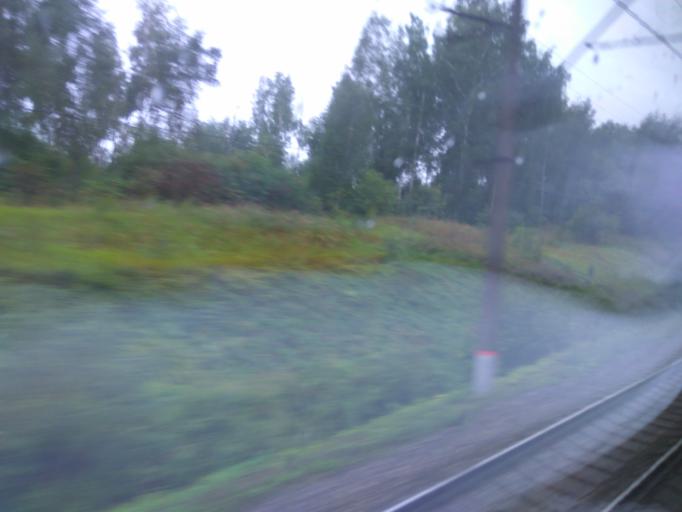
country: RU
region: Moskovskaya
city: Ozery
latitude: 54.7187
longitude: 38.4338
